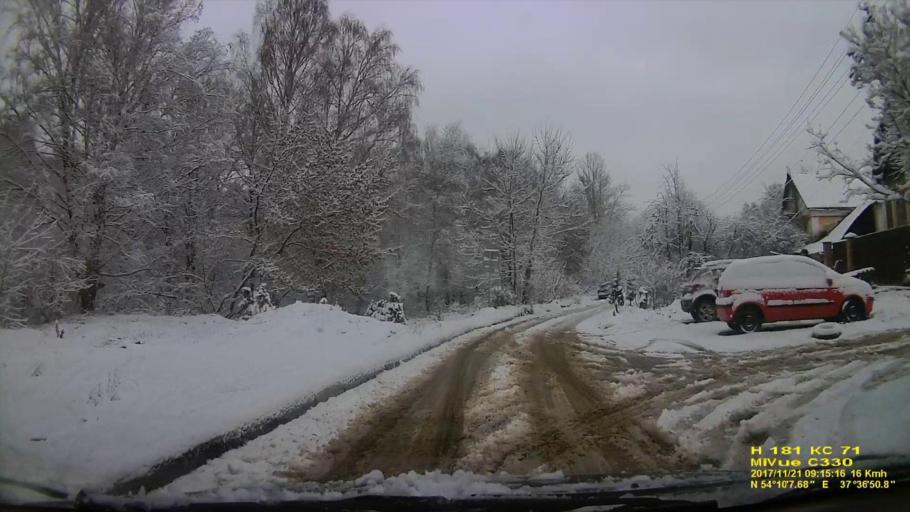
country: RU
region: Tula
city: Tula
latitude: 54.1688
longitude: 37.6141
